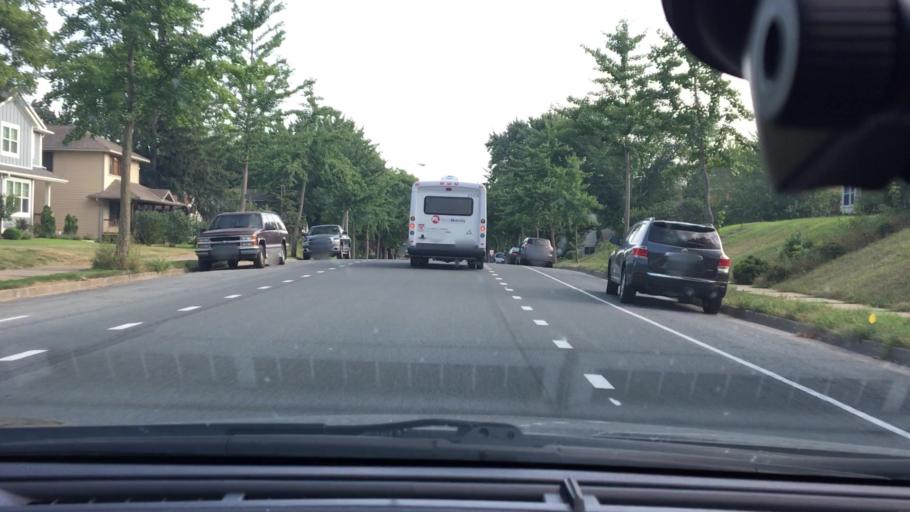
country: US
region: Minnesota
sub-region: Hennepin County
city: Richfield
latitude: 44.9119
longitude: -93.2524
